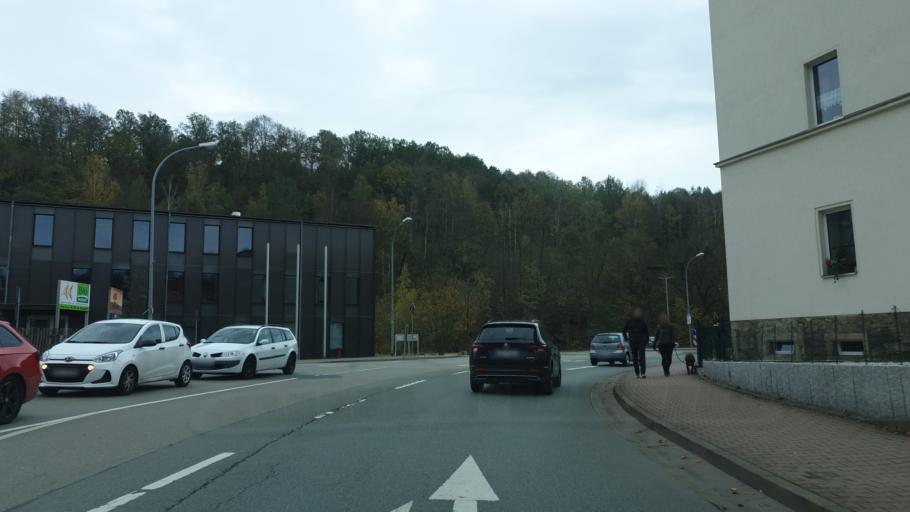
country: DE
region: Saxony
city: Schwarzenberg
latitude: 50.5378
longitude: 12.7895
